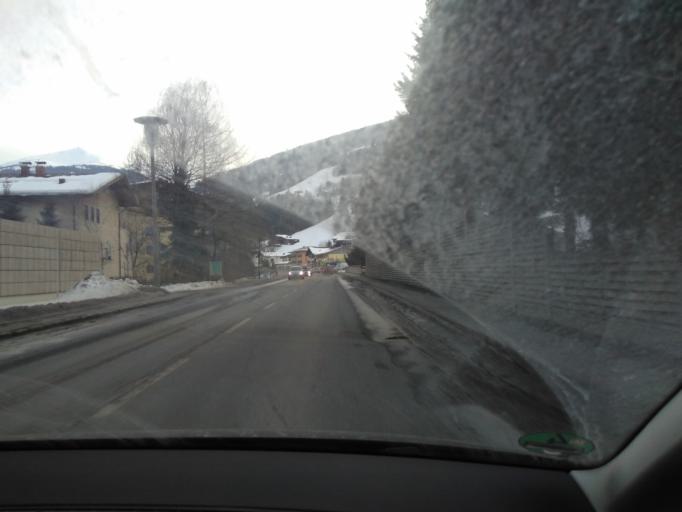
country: AT
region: Salzburg
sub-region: Politischer Bezirk Sankt Johann im Pongau
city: Bad Hofgastein
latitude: 47.1735
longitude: 13.0986
